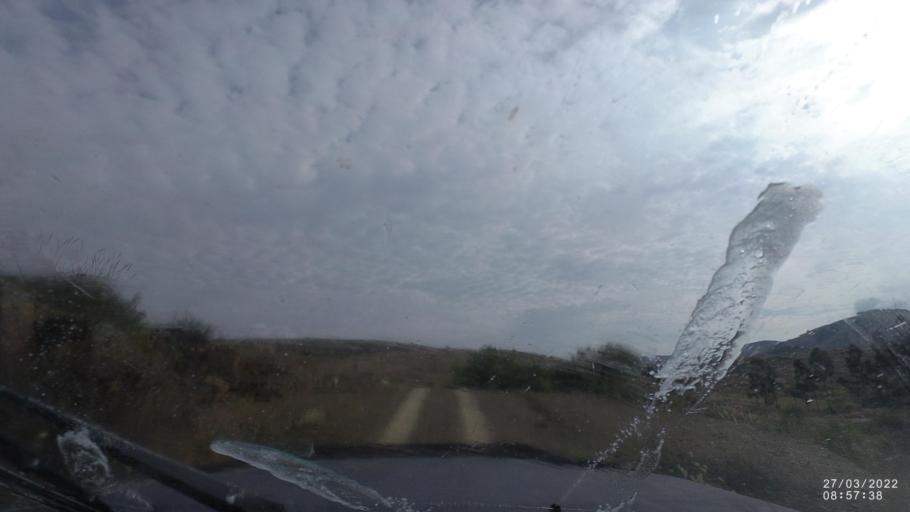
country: BO
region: Cochabamba
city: Cliza
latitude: -17.7460
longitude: -65.8577
